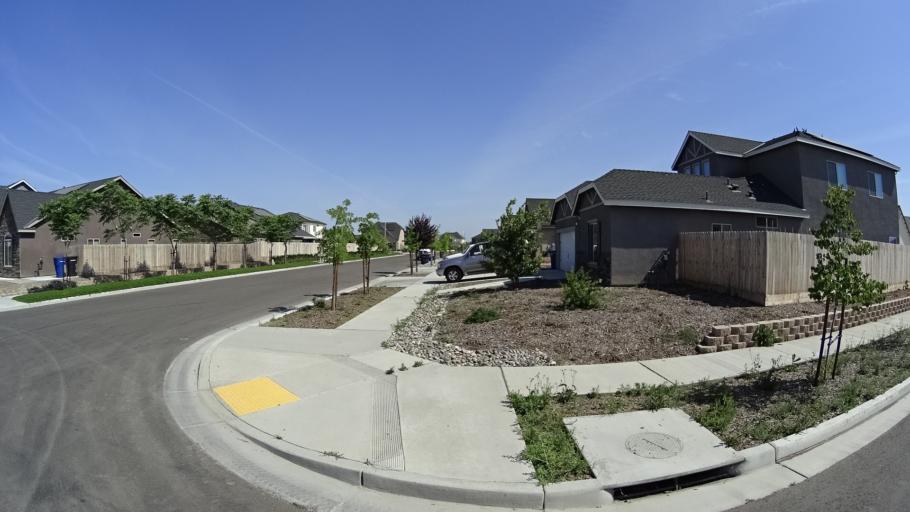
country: US
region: California
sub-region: Kings County
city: Hanford
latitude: 36.3368
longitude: -119.6792
